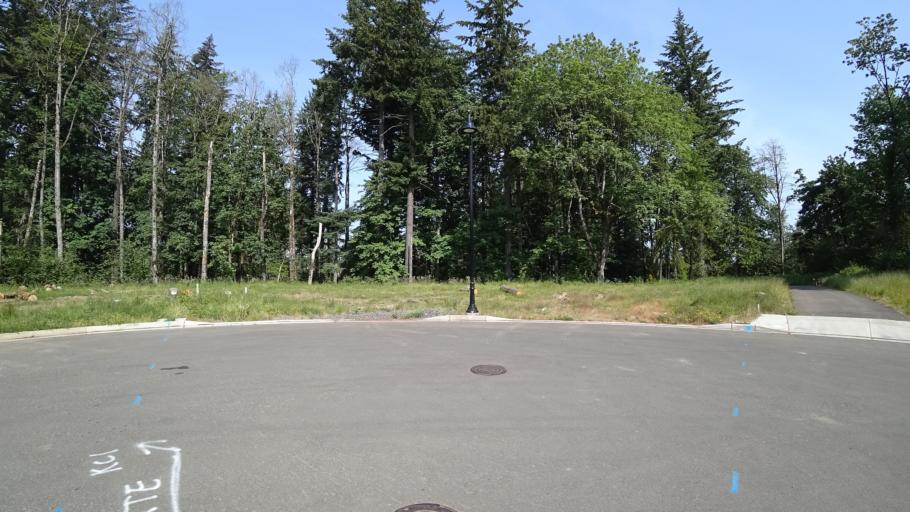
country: US
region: Oregon
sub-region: Clackamas County
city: Happy Valley
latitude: 45.4518
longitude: -122.5048
